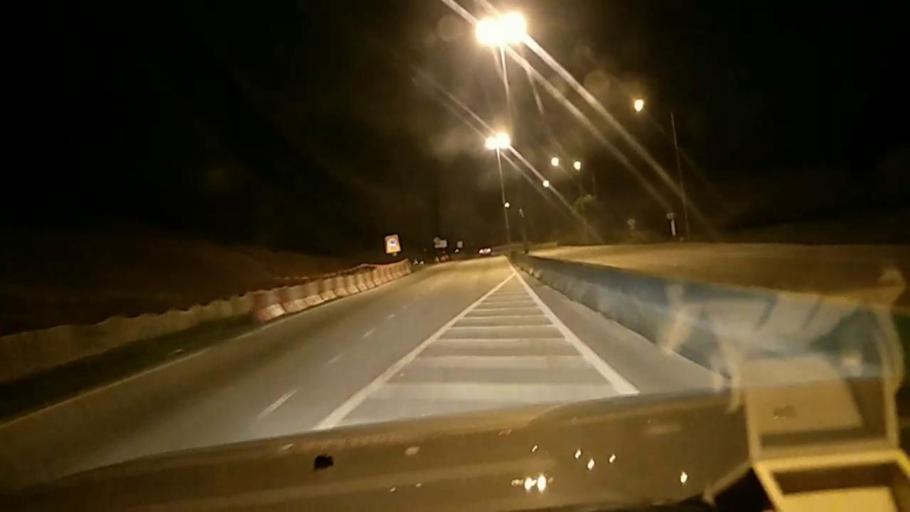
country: MY
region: Selangor
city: Kampung Baru Subang
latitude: 3.1319
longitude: 101.5038
